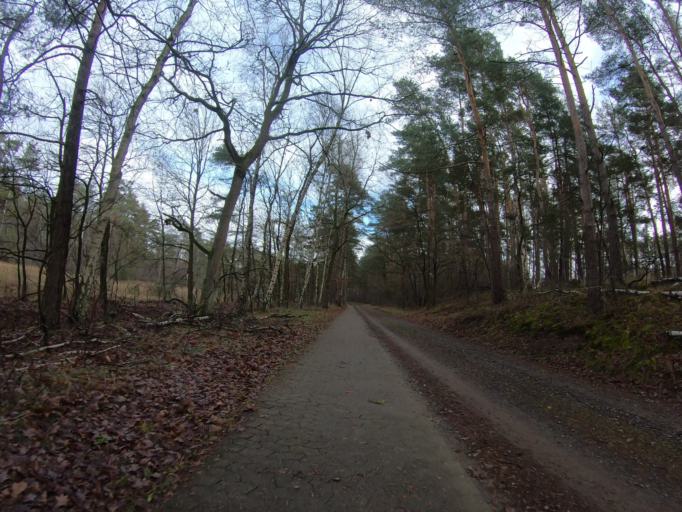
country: DE
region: Lower Saxony
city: Wagenhoff
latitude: 52.4902
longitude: 10.5065
